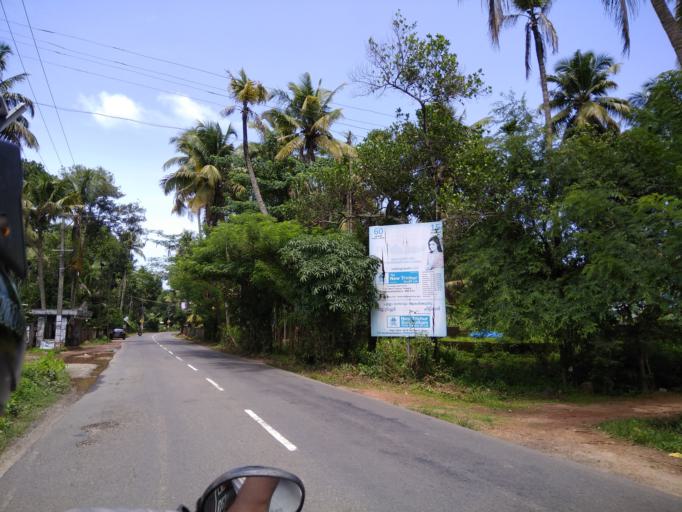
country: IN
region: Kerala
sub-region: Thrissur District
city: Thanniyam
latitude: 10.4884
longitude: 76.1364
